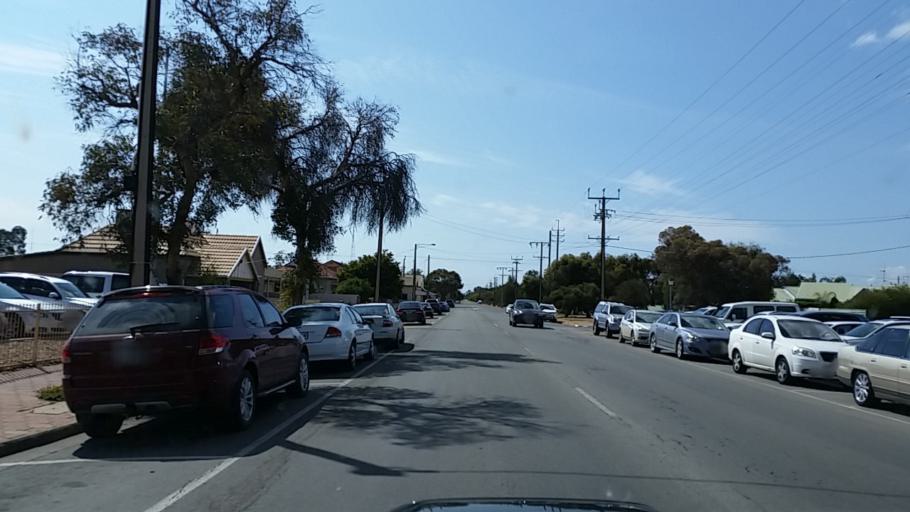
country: AU
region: South Australia
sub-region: Port Pirie City and Dists
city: Port Pirie
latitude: -33.1768
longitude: 138.0039
